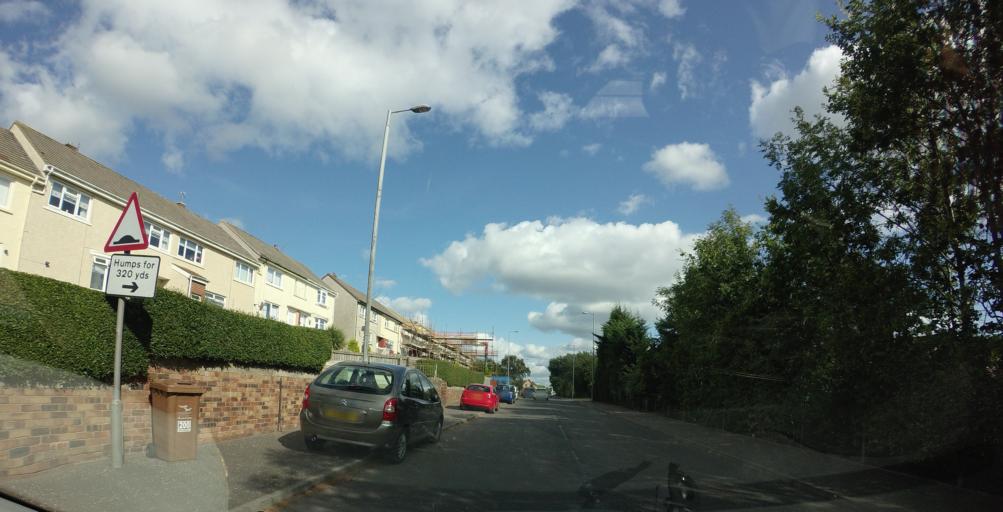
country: GB
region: Scotland
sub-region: North Lanarkshire
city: Coatbridge
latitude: 55.8446
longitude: -4.0446
